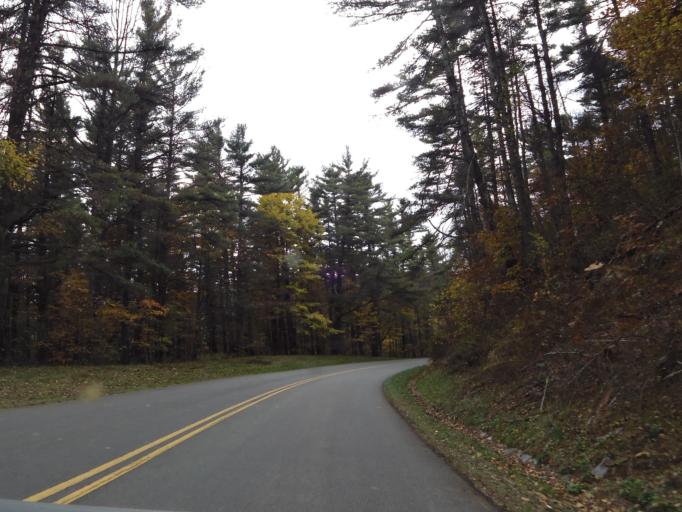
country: US
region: North Carolina
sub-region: Ashe County
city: Jefferson
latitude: 36.3724
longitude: -81.3329
